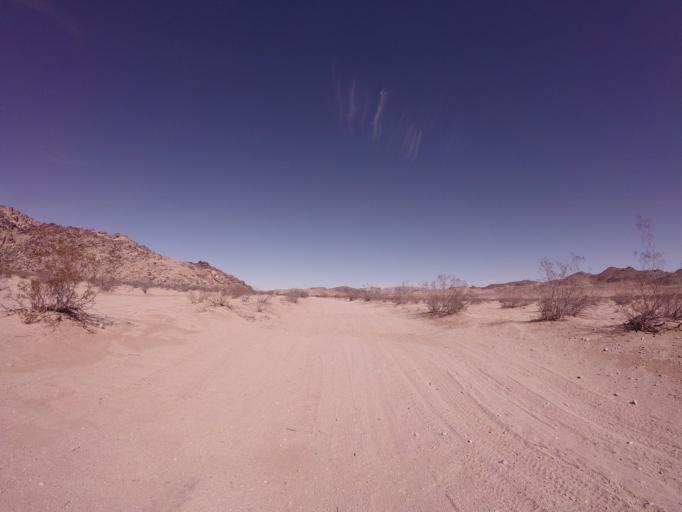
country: US
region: California
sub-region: San Bernardino County
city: Joshua Tree
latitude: 34.3239
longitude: -116.3885
